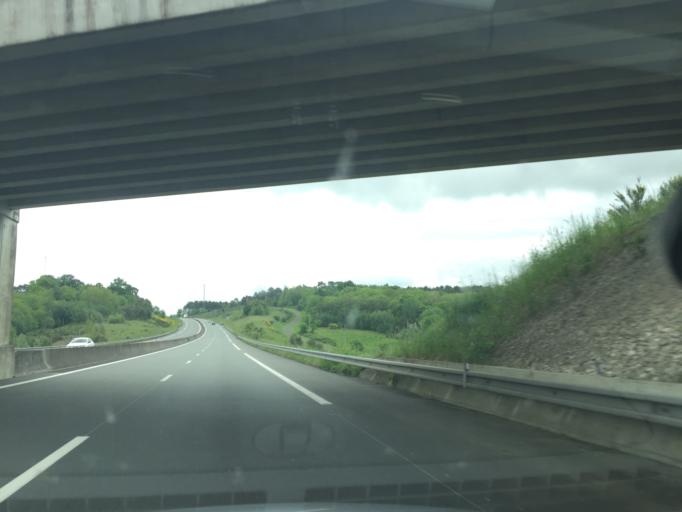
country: FR
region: Pays de la Loire
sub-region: Departement de la Sarthe
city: Luceau
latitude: 47.7136
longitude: 0.3462
